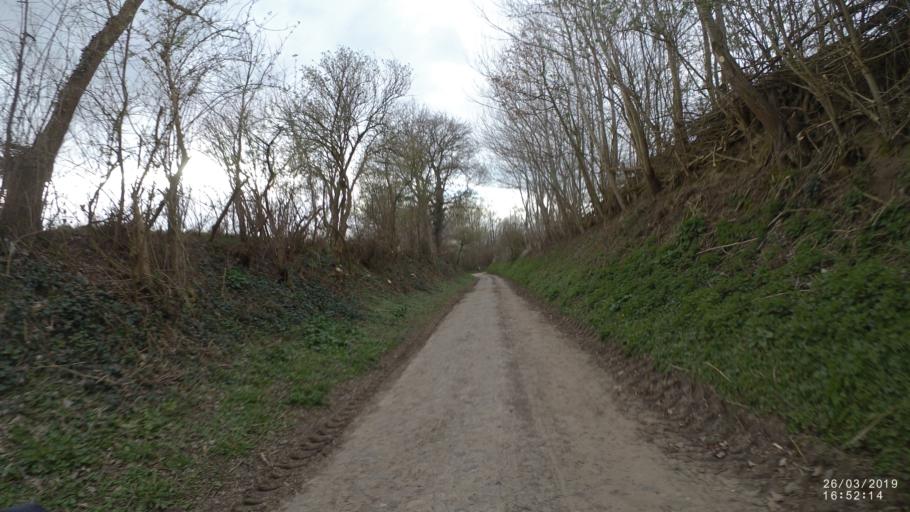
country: BE
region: Flanders
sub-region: Provincie Vlaams-Brabant
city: Bertem
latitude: 50.8403
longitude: 4.6328
